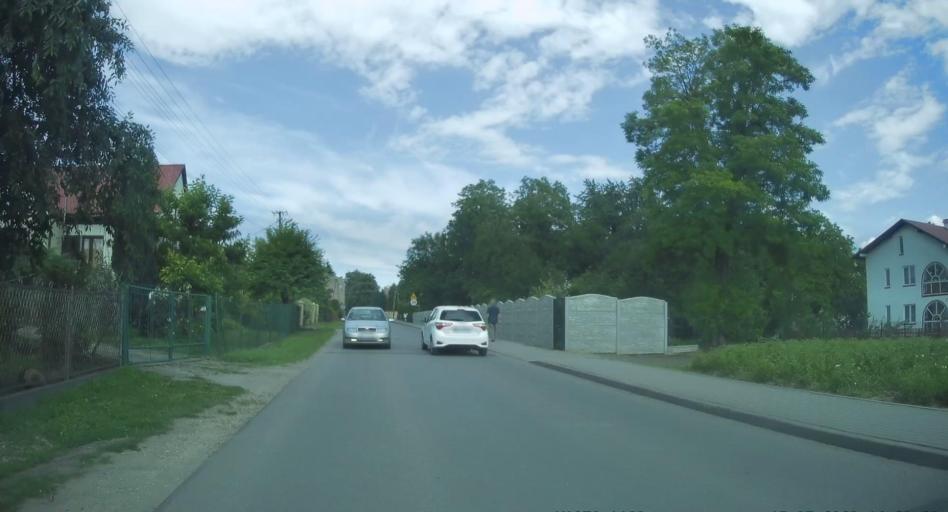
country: PL
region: Subcarpathian Voivodeship
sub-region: Powiat przemyski
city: Zurawica
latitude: 49.8129
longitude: 22.8481
